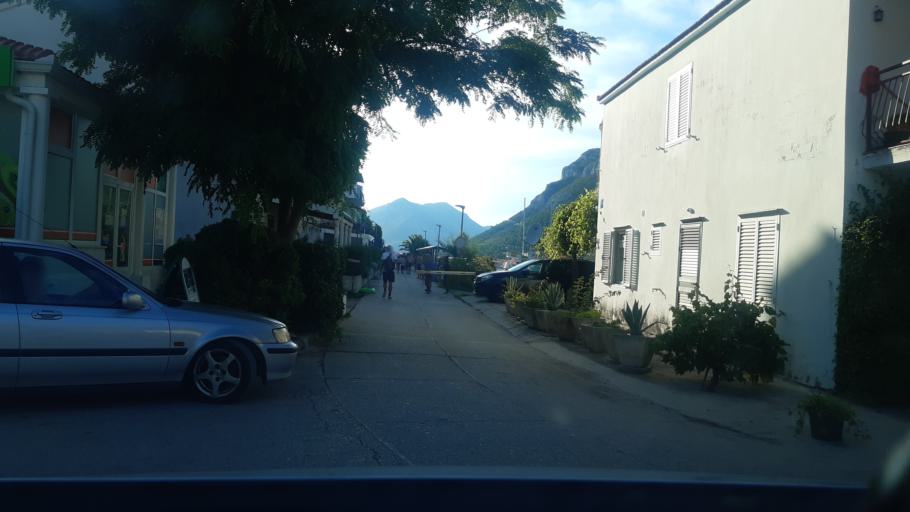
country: HR
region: Dubrovacko-Neretvanska
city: Blato
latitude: 42.8899
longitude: 17.4536
